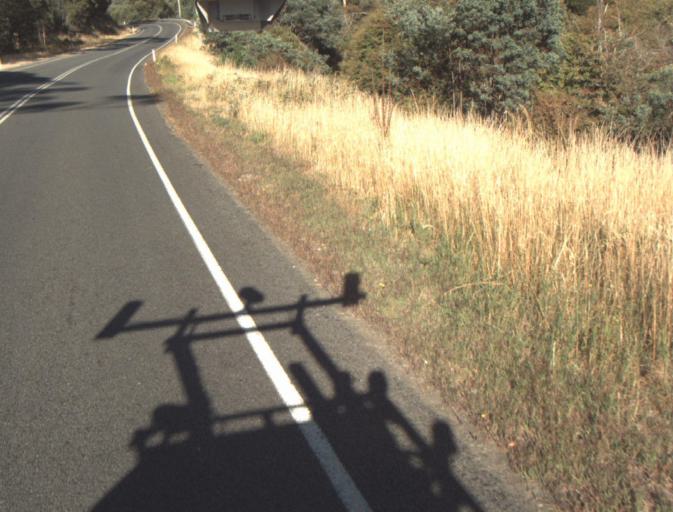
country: AU
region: Tasmania
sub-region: Launceston
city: Newstead
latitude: -41.4187
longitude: 147.2787
